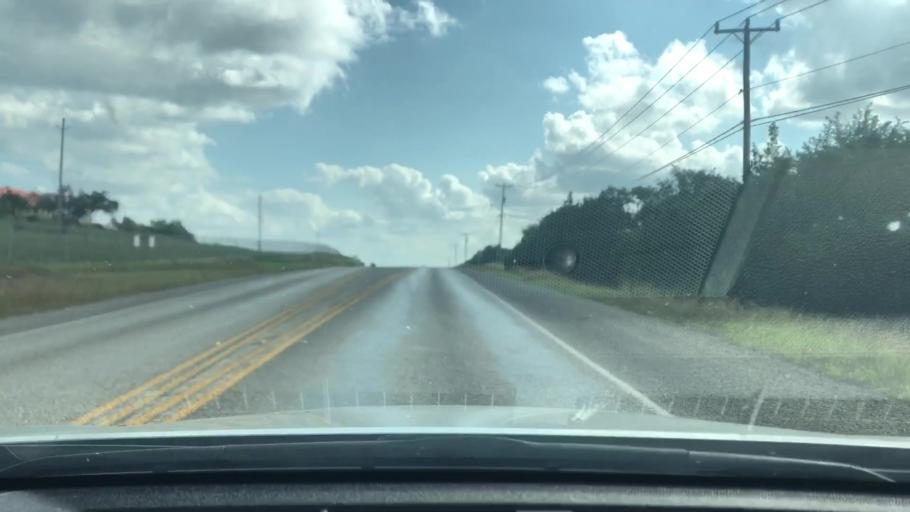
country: US
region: Texas
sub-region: Bexar County
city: Scenic Oaks
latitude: 29.6968
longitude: -98.6315
